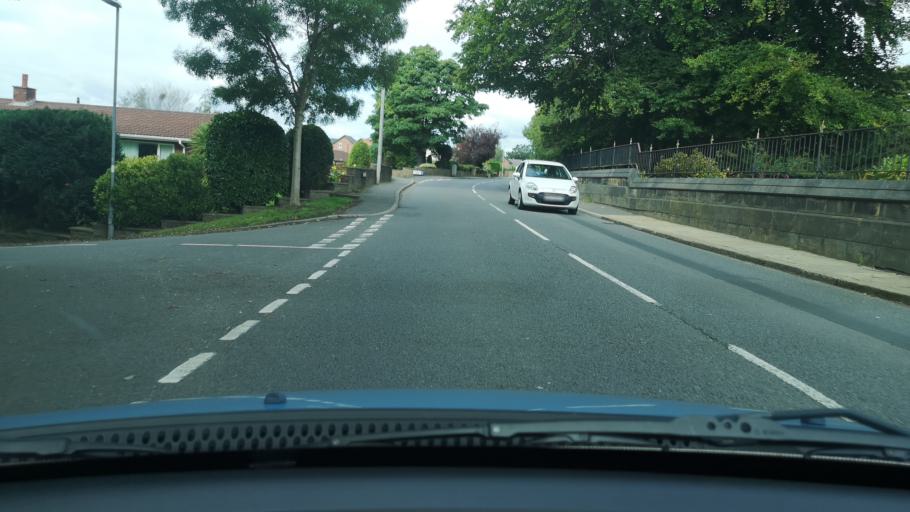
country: GB
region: England
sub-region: Kirklees
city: Mirfield
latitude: 53.6794
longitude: -1.6814
